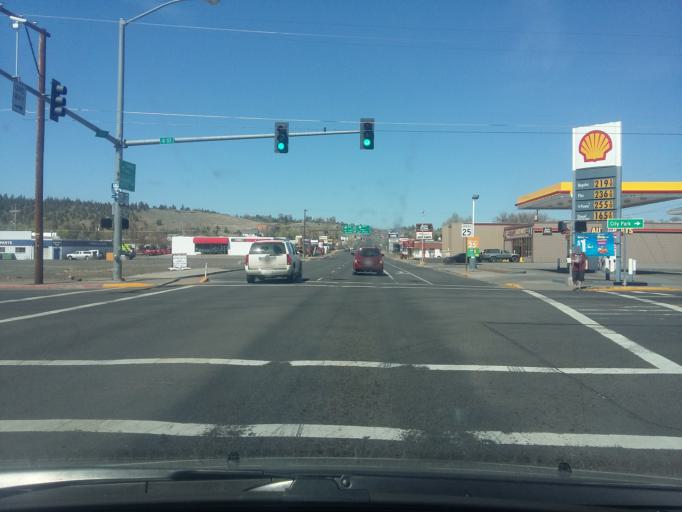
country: US
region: Oregon
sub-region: Jefferson County
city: Madras
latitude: 44.6358
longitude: -121.1296
